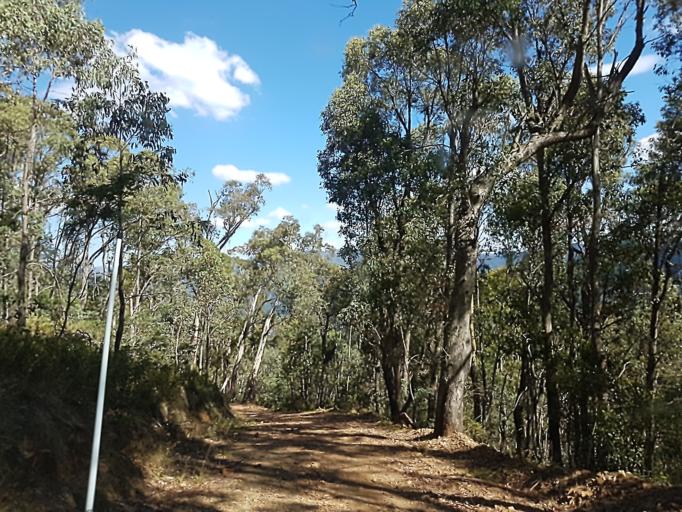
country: AU
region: Victoria
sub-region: Alpine
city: Mount Beauty
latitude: -36.8902
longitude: 147.0260
